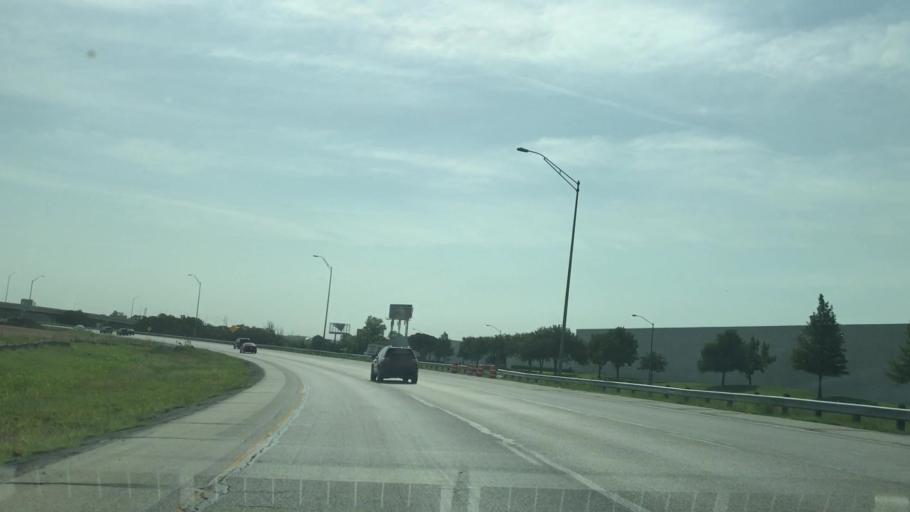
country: US
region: Texas
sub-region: Tarrant County
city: Euless
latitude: 32.8357
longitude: -97.0445
